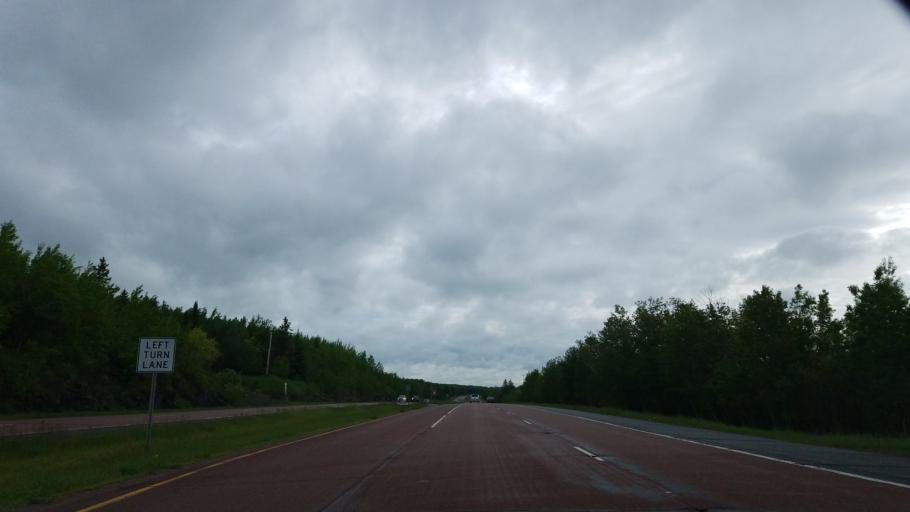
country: US
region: Minnesota
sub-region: Saint Louis County
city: Arnold
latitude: 46.8503
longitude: -91.9909
